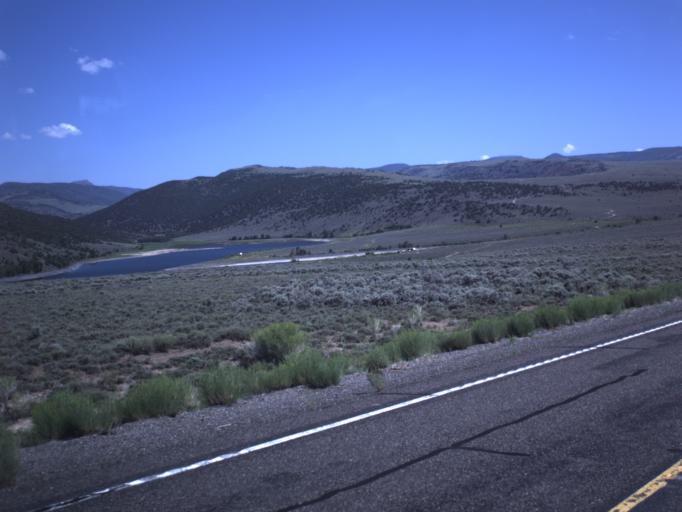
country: US
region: Utah
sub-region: Wayne County
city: Loa
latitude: 38.5138
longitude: -111.5248
